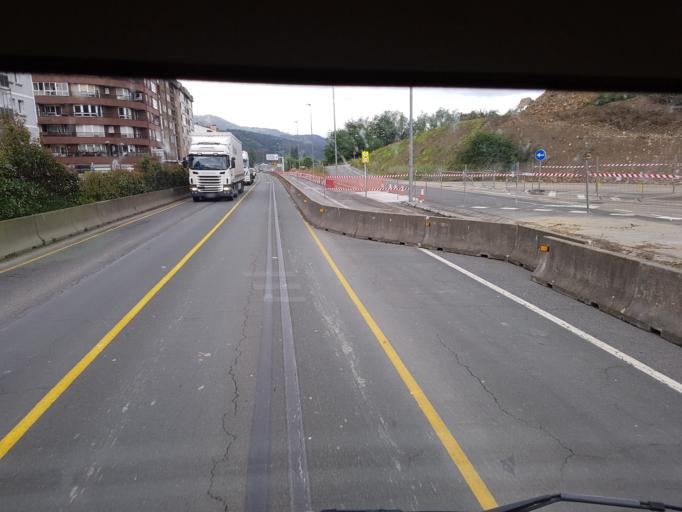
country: ES
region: Basque Country
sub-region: Bizkaia
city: Durango
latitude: 43.1752
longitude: -2.6367
